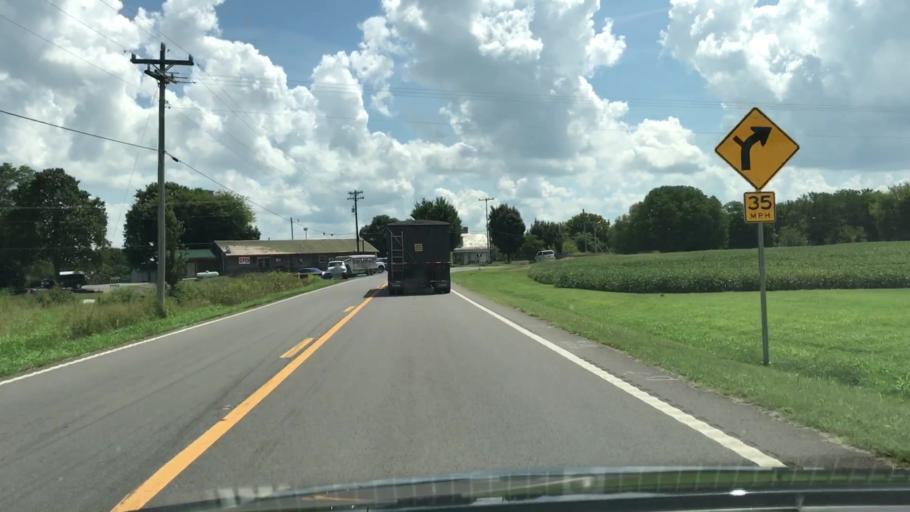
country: US
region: Tennessee
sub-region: Robertson County
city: Springfield
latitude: 36.6022
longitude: -86.9202
